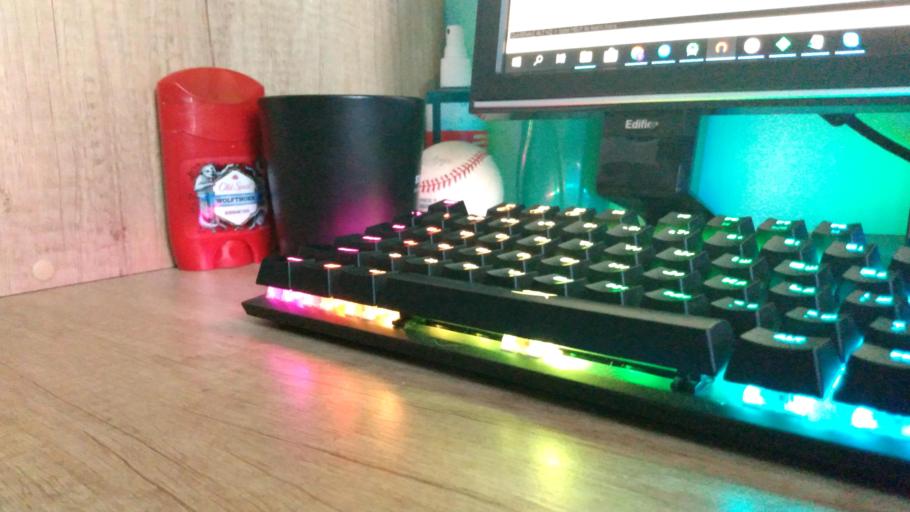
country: RU
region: Moskovskaya
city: Pushchino
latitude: 54.8088
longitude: 37.5687
